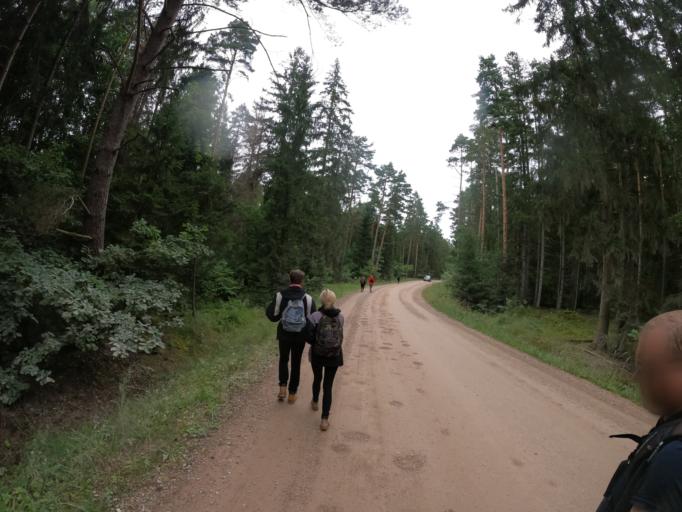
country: LV
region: Kuldigas Rajons
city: Kuldiga
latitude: 56.9908
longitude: 21.9740
